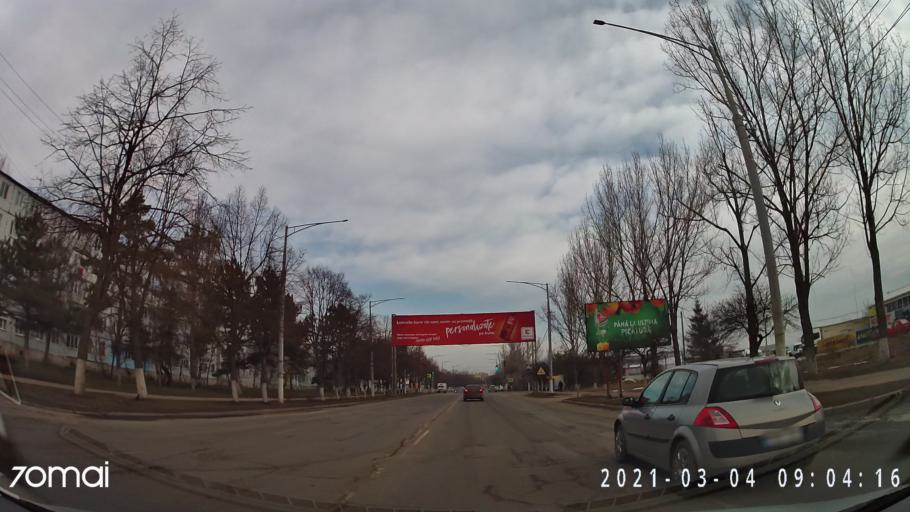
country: MD
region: Balti
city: Balti
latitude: 47.7568
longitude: 27.9412
